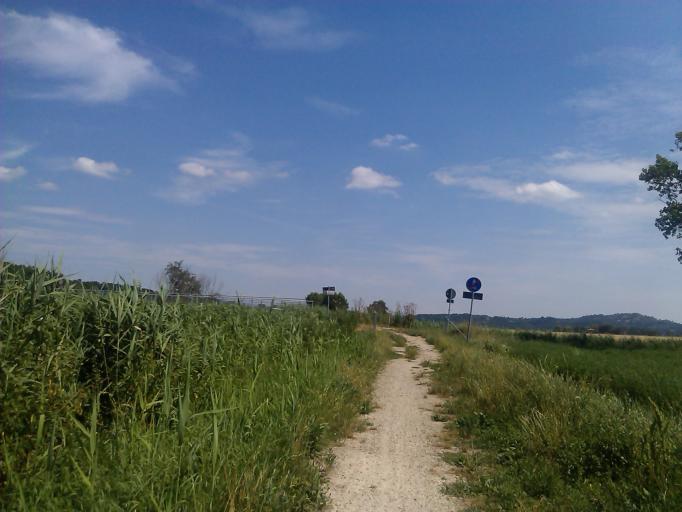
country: IT
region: Umbria
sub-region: Provincia di Perugia
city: Pozzuolo
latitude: 43.0735
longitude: 11.9240
